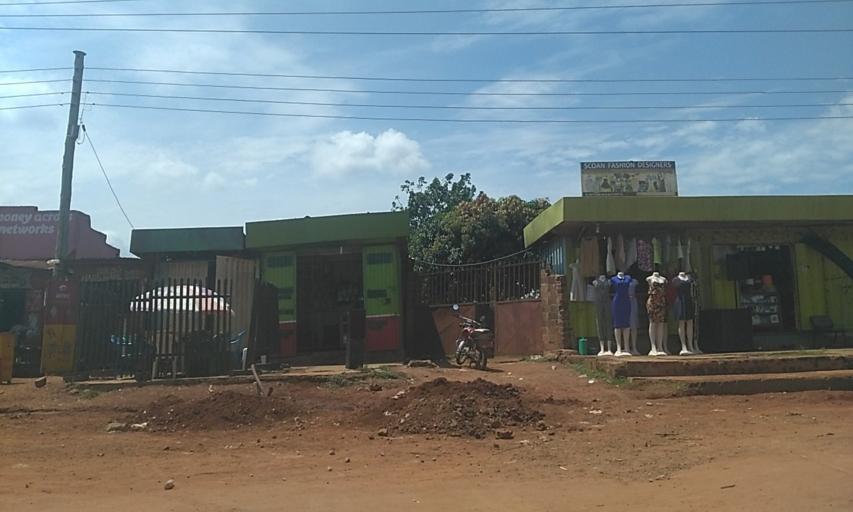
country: UG
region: Central Region
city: Kampala Central Division
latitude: 0.3629
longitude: 32.5296
